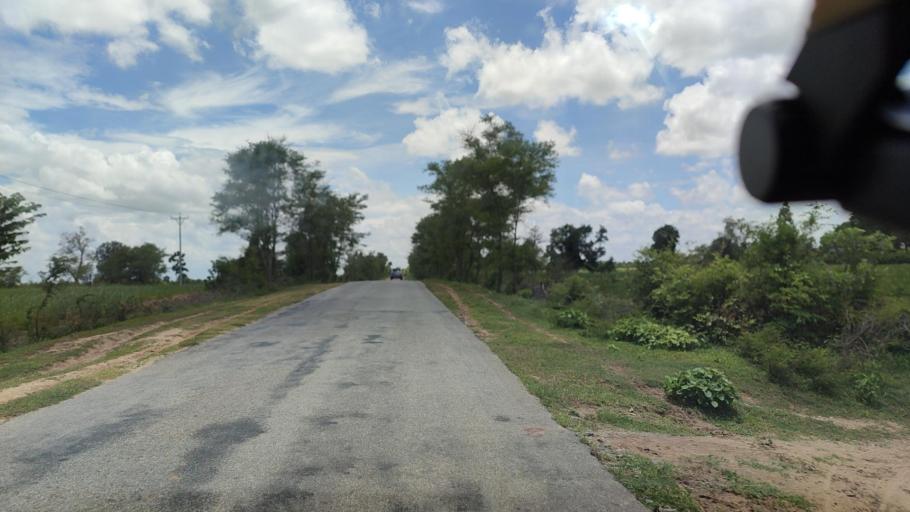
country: MM
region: Magway
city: Taungdwingyi
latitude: 20.2003
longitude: 95.3167
